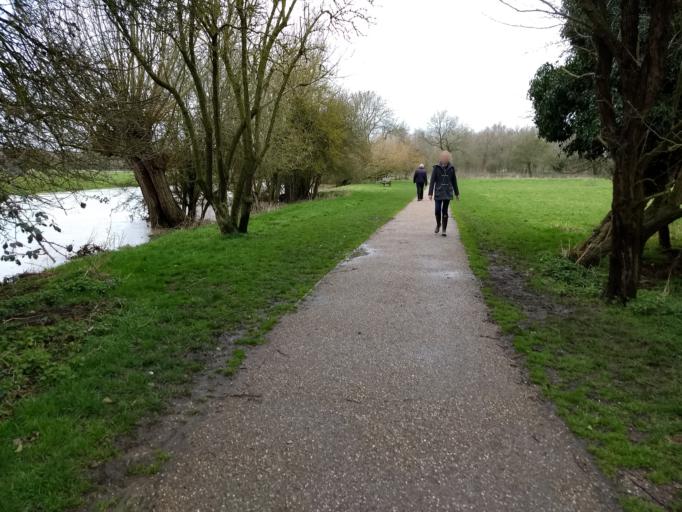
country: GB
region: England
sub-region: Milton Keynes
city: Stony Stratford
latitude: 52.0575
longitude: -0.8597
